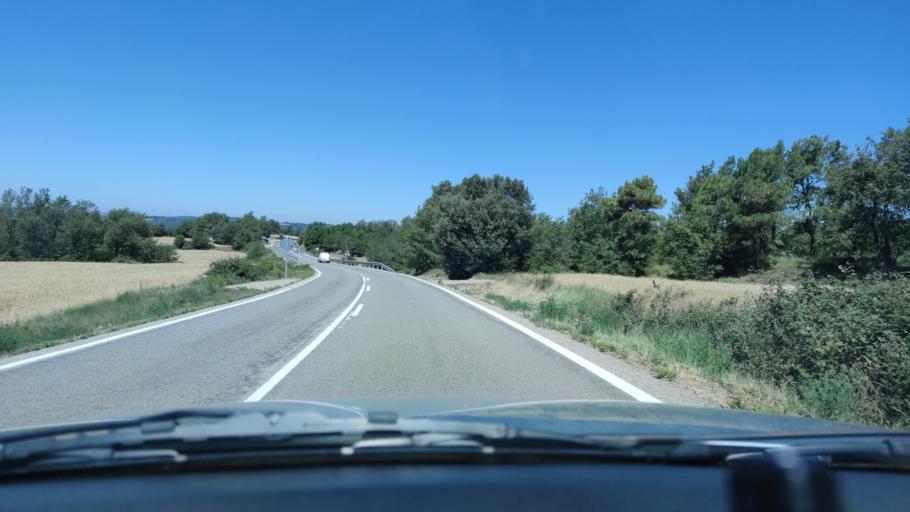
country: ES
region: Catalonia
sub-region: Provincia de Lleida
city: Solsona
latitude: 41.8958
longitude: 1.5468
